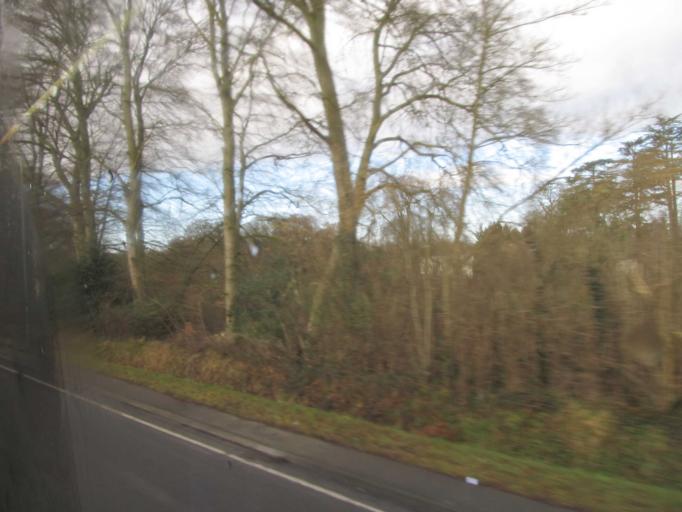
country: GB
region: England
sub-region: Hampshire
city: Basingstoke
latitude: 51.2460
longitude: -1.1246
